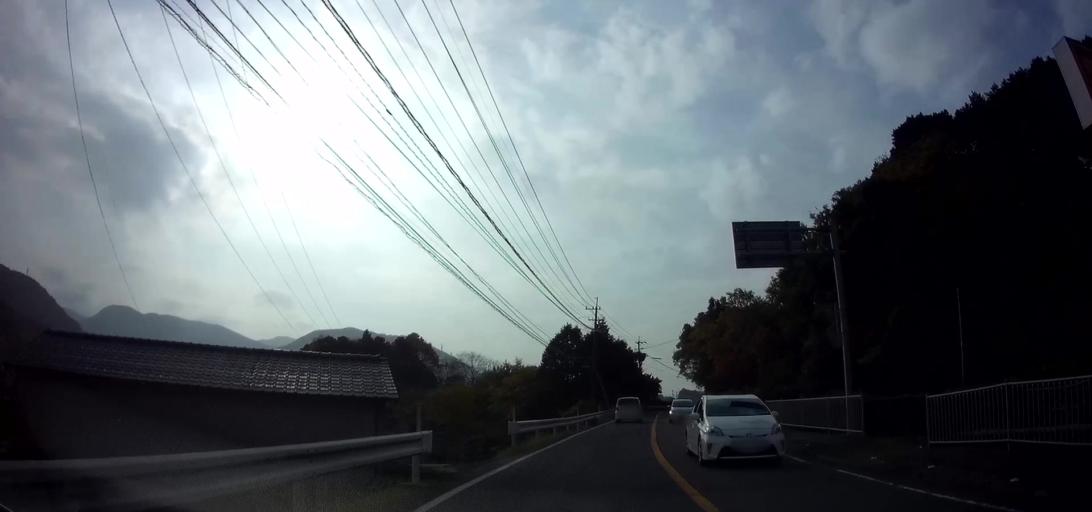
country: JP
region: Nagasaki
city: Shimabara
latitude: 32.7713
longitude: 130.2144
